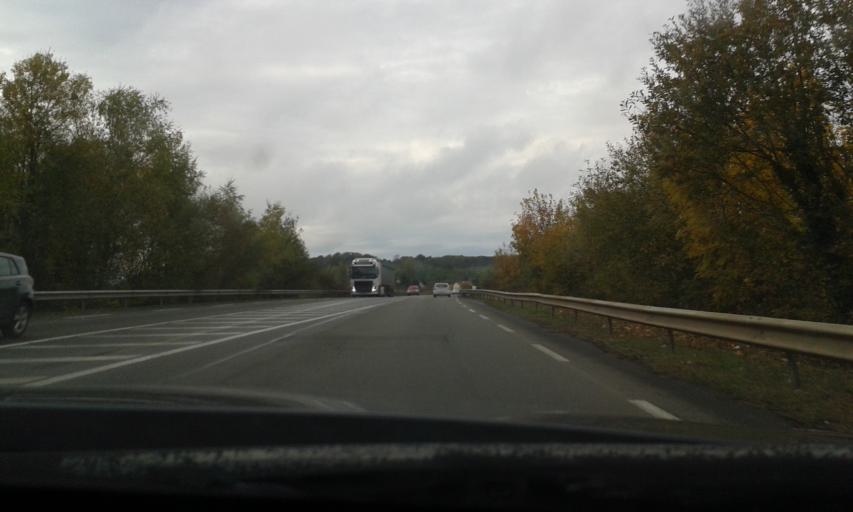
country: FR
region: Centre
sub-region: Departement d'Eure-et-Loir
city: Saint-Lubin-des-Joncherets
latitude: 48.7626
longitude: 1.2258
